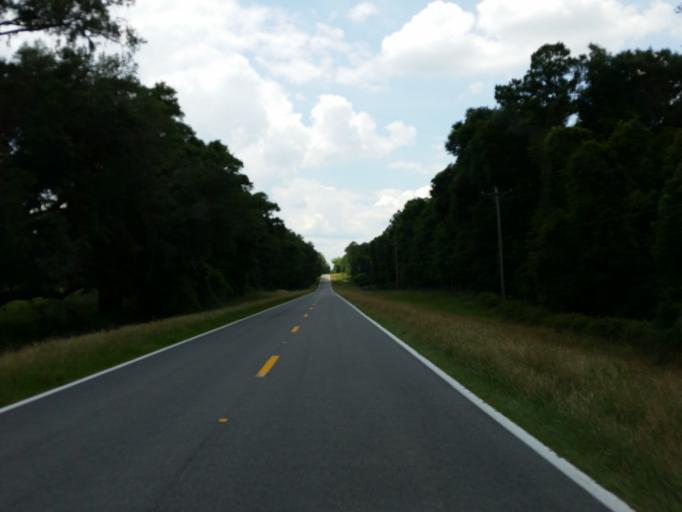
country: US
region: Florida
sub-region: Alachua County
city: High Springs
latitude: 29.9524
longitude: -82.5972
